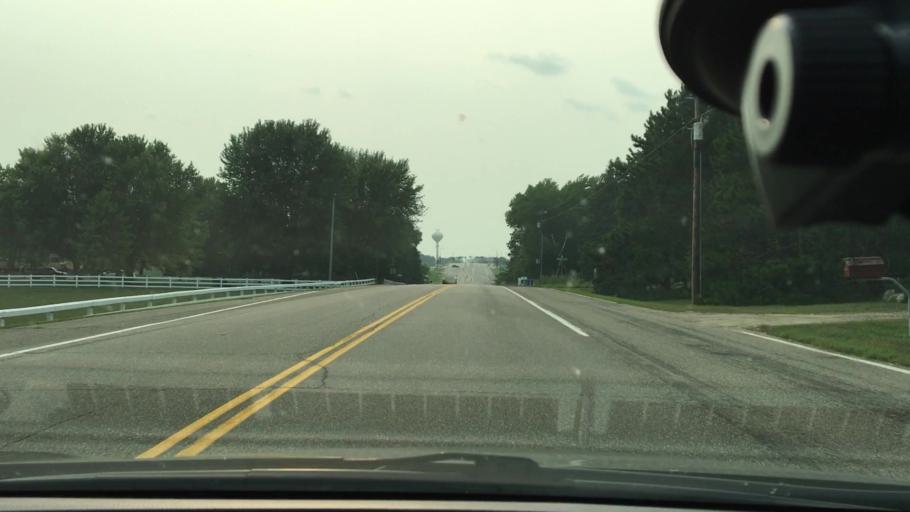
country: US
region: Minnesota
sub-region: Hennepin County
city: Dayton
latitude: 45.2524
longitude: -93.5460
